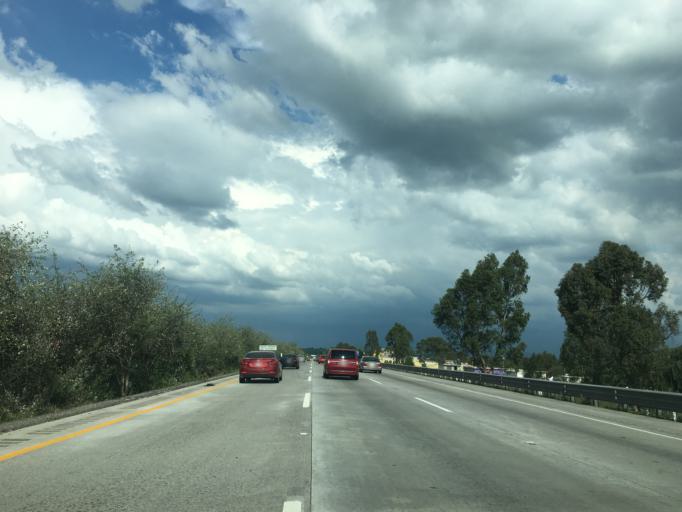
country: MX
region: Mexico
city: San Francisco Soyaniquilpan
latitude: 19.9933
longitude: -99.4731
